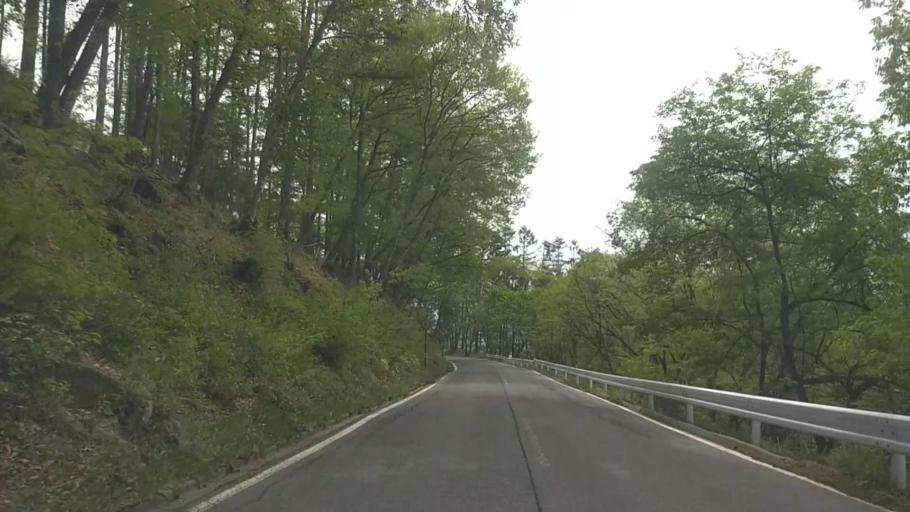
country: JP
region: Nagano
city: Chino
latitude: 36.0436
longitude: 138.2691
